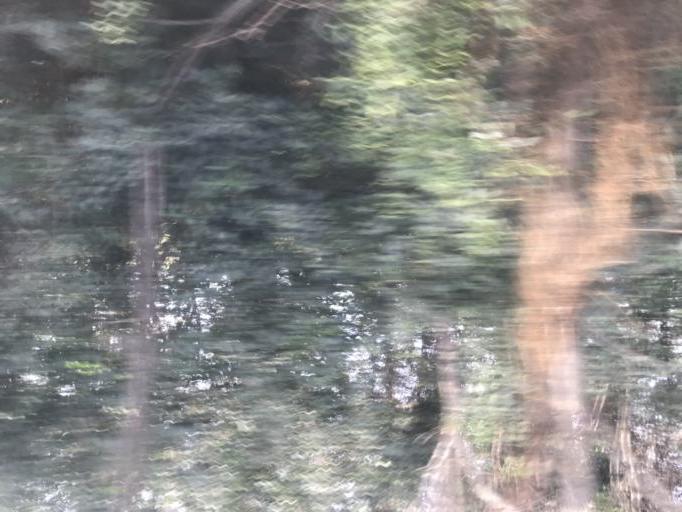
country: AR
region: Cordoba
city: Laguna Larga
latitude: -31.7962
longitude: -63.7862
